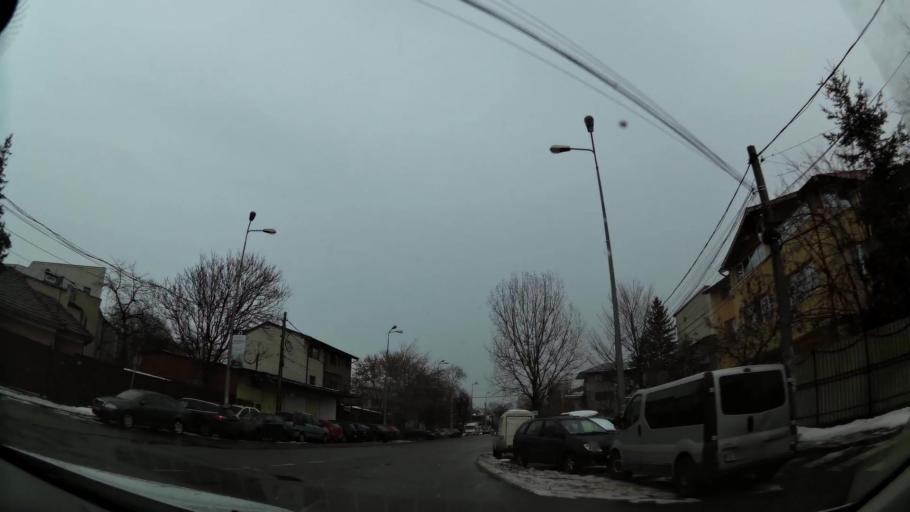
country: RO
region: Ilfov
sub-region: Comuna Chiajna
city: Rosu
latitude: 44.4724
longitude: 26.0557
